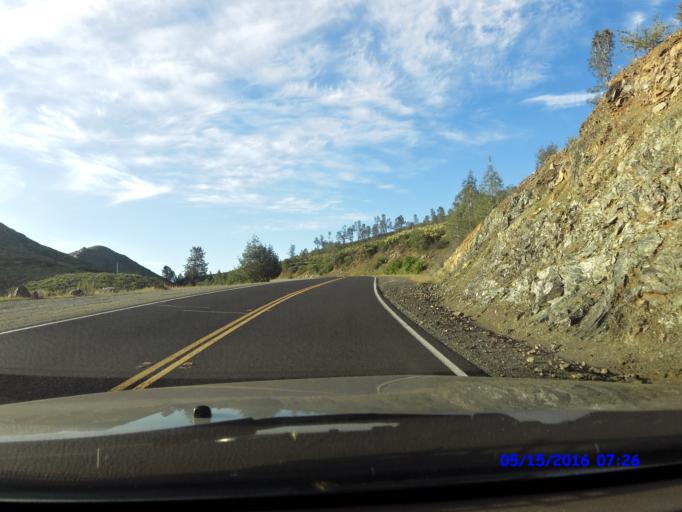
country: US
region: California
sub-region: Tuolumne County
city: Tuolumne City
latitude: 37.7538
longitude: -120.2481
